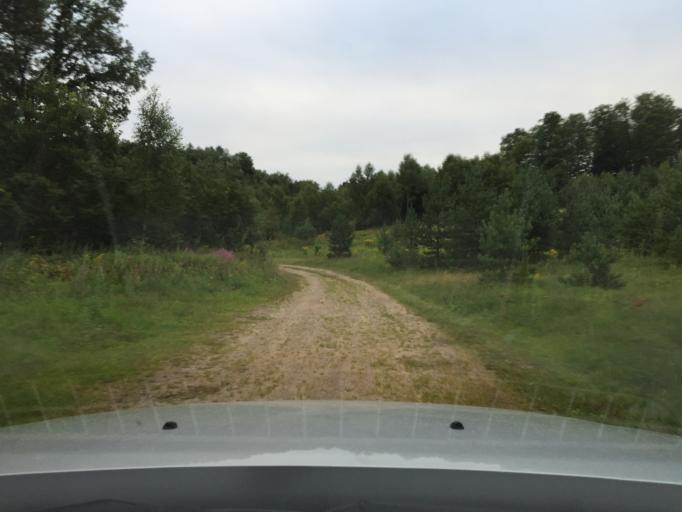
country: SE
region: Skane
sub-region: Hassleholms Kommun
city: Sosdala
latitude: 56.0440
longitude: 13.6990
